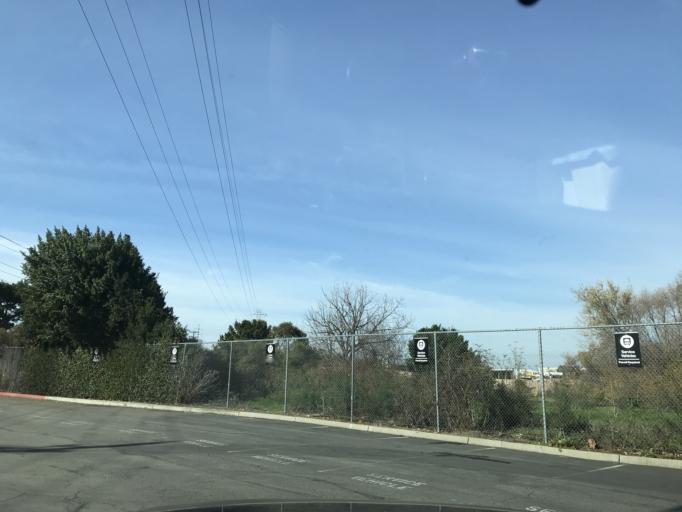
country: US
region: California
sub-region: San Mateo County
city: East Palo Alto
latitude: 37.4806
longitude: -122.1453
